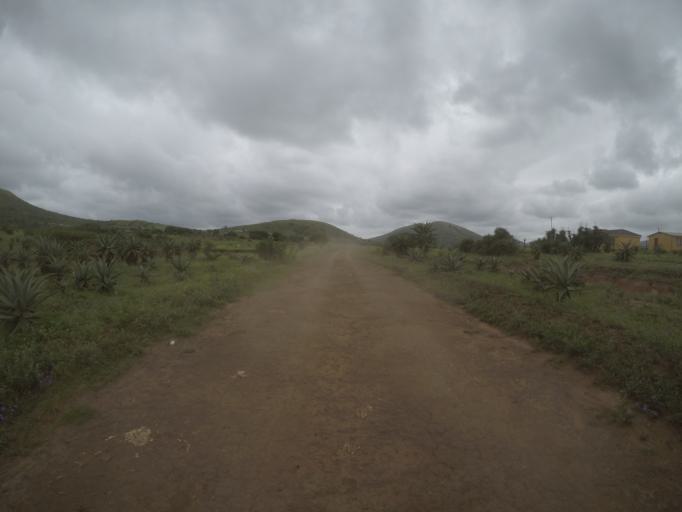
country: ZA
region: KwaZulu-Natal
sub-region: uThungulu District Municipality
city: Empangeni
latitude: -28.6074
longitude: 31.8652
